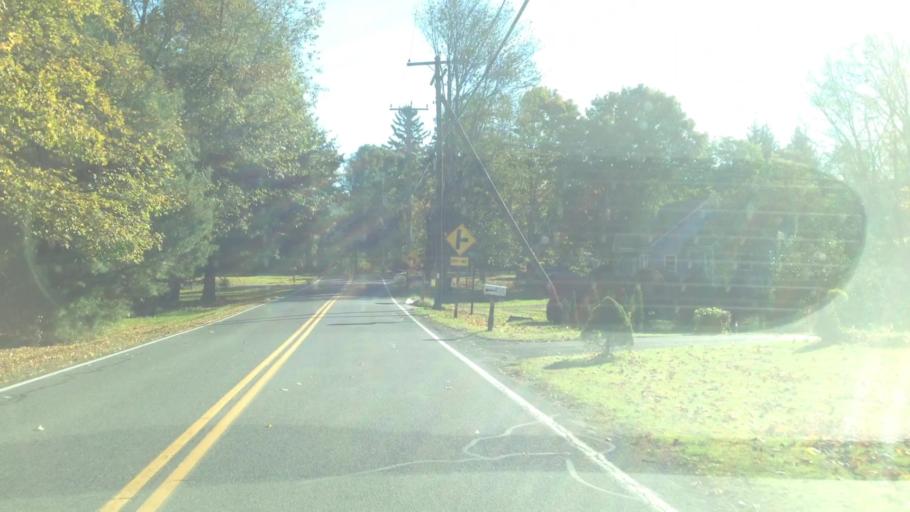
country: US
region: New York
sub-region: Ulster County
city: Port Ewen
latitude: 41.8561
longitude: -73.9781
